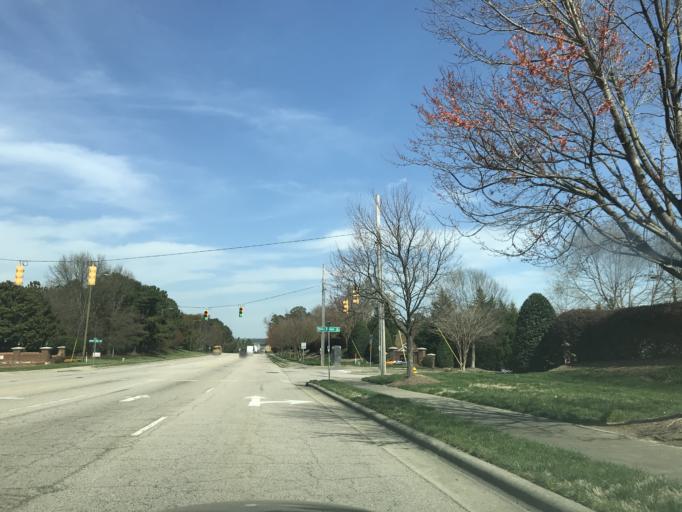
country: US
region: North Carolina
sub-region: Wake County
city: Knightdale
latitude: 35.8324
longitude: -78.5606
